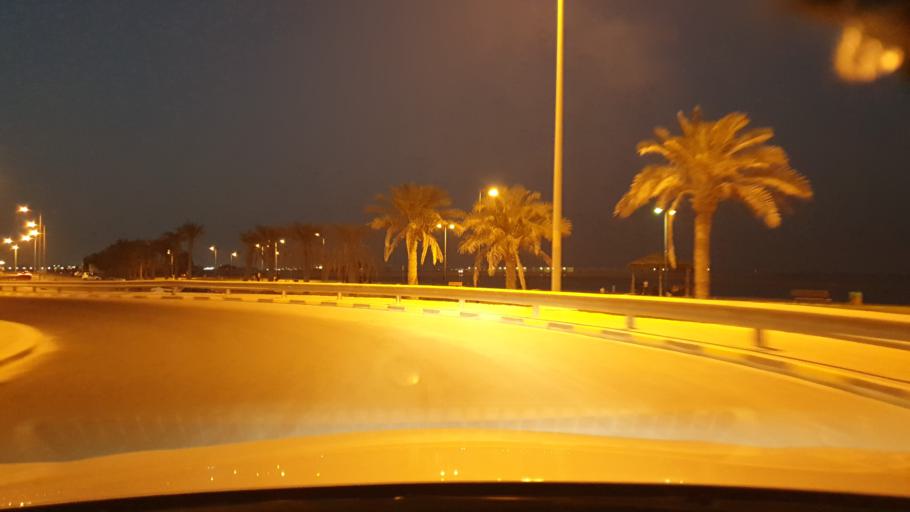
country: BH
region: Northern
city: Ar Rifa'
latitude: 26.0480
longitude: 50.6202
